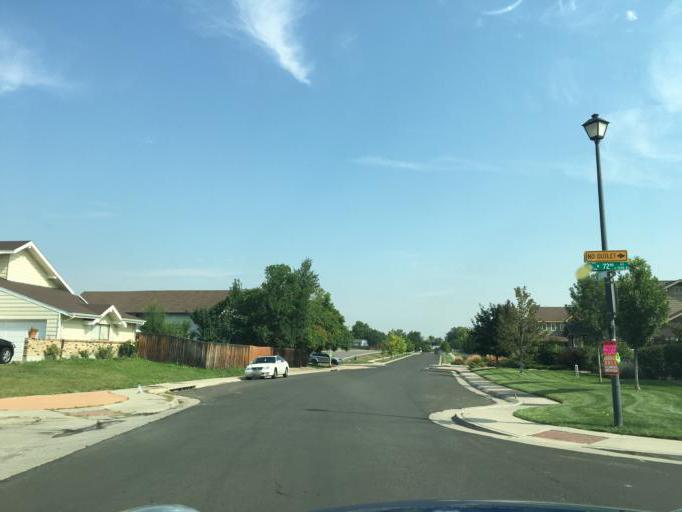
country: US
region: Colorado
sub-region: Adams County
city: Westminster
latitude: 39.8282
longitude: -105.0587
